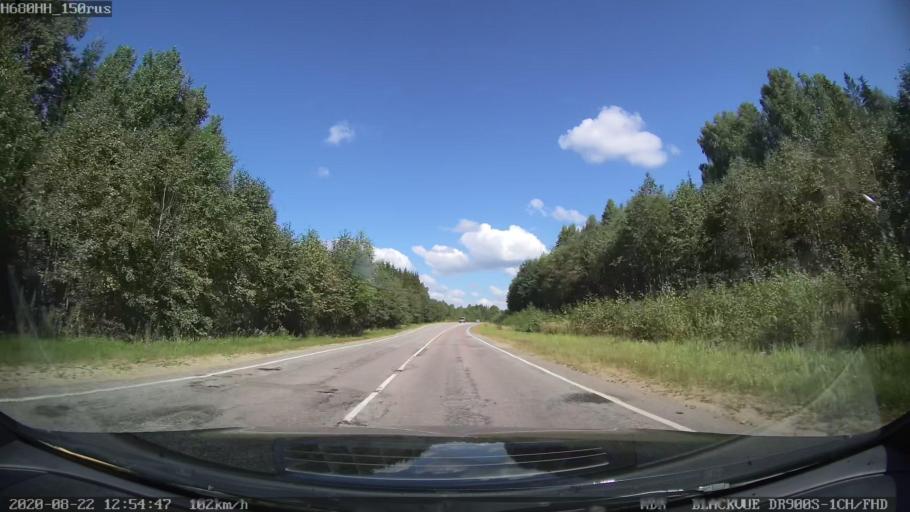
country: RU
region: Tverskaya
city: Rameshki
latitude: 57.5361
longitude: 36.2896
